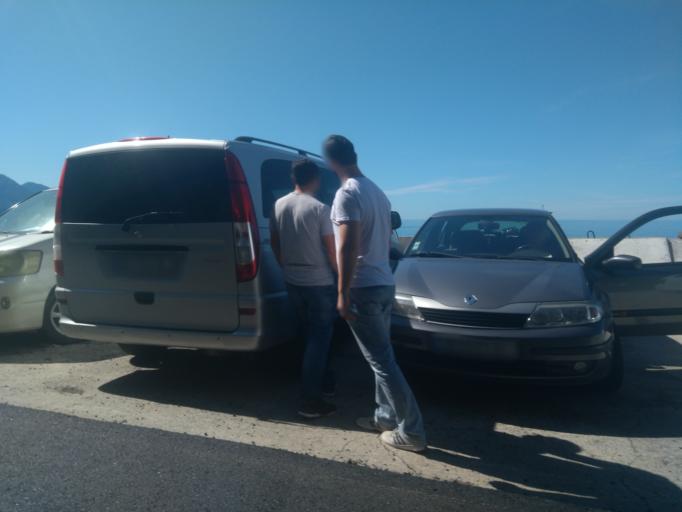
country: TR
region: Artvin
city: Kemalpasa
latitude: 41.5267
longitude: 41.5490
